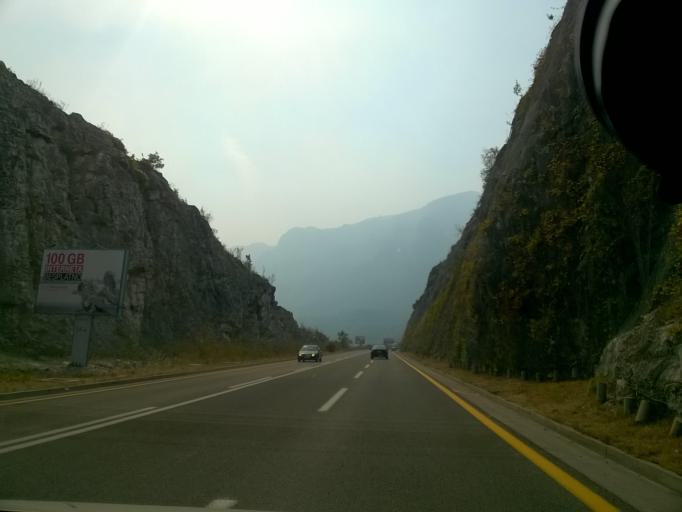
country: ME
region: Bar
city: Sutomore
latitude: 42.2085
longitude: 19.0489
